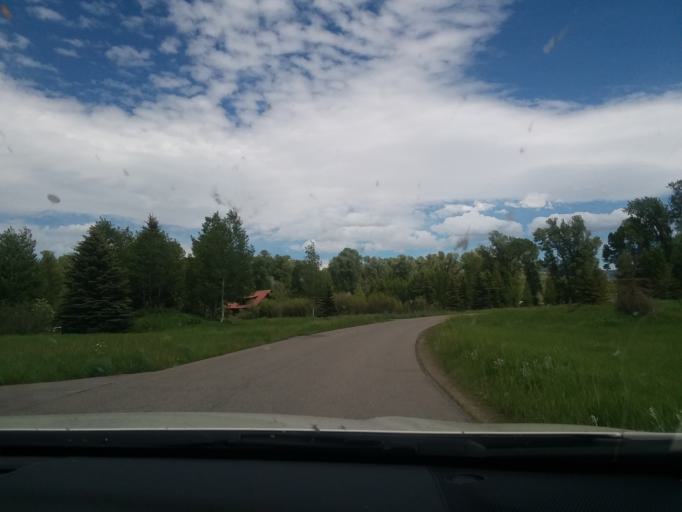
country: US
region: Wyoming
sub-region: Teton County
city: Moose Wilson Road
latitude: 43.5046
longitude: -110.8507
